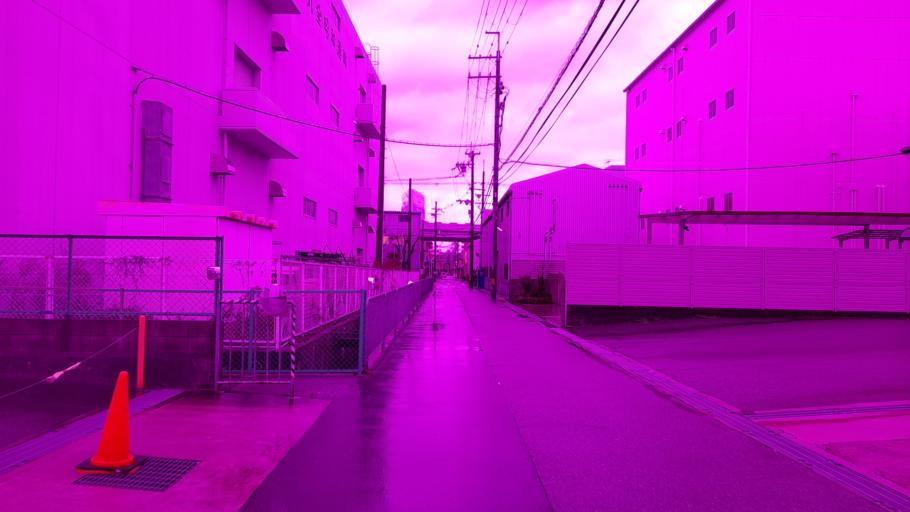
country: JP
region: Osaka
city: Toyonaka
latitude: 34.7676
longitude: 135.4586
